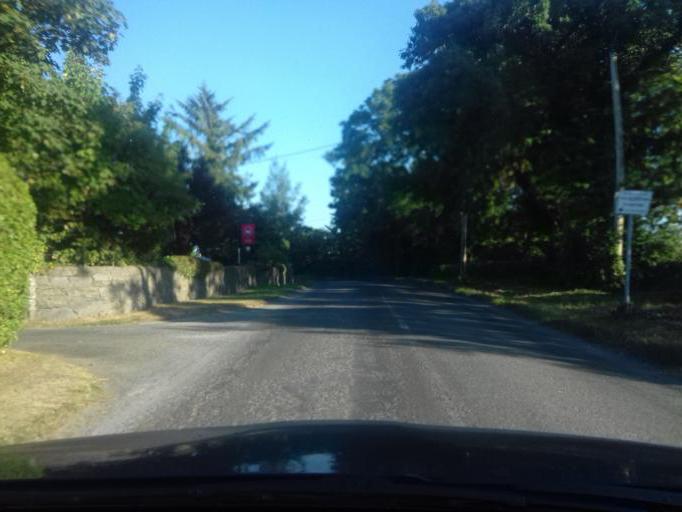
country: IE
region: Leinster
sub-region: Dublin City
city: Finglas
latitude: 53.4460
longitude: -6.3051
